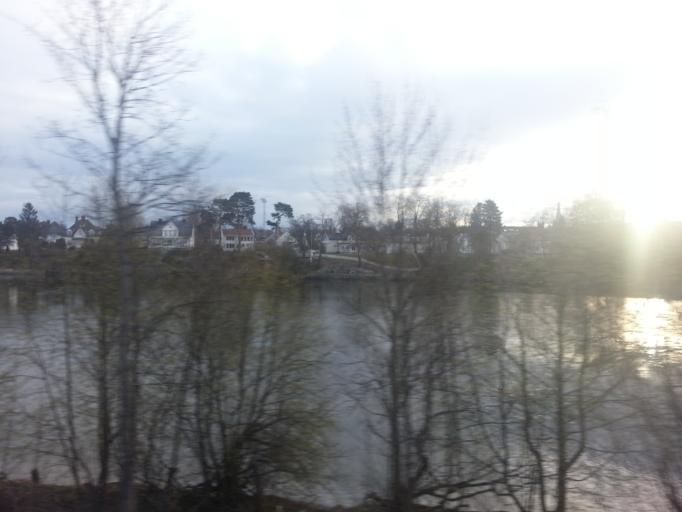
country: NO
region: Sor-Trondelag
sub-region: Trondheim
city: Trondheim
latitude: 63.4233
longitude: 10.3769
